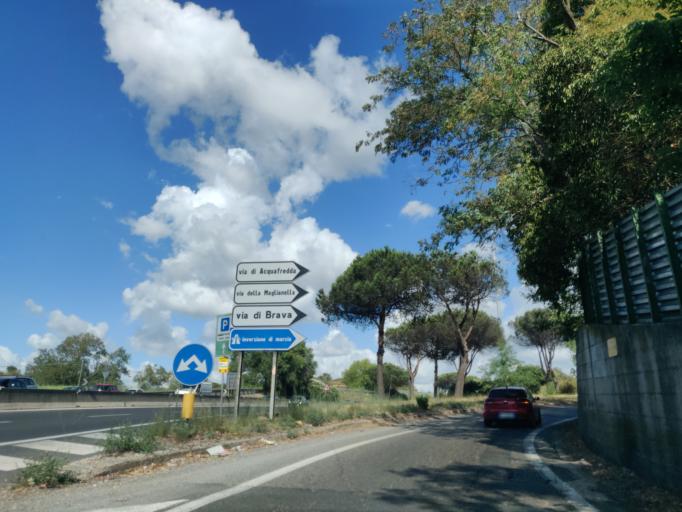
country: IT
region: Latium
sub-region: Citta metropolitana di Roma Capitale
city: La Massimina-Casal Lumbroso
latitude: 41.8862
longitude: 12.3856
